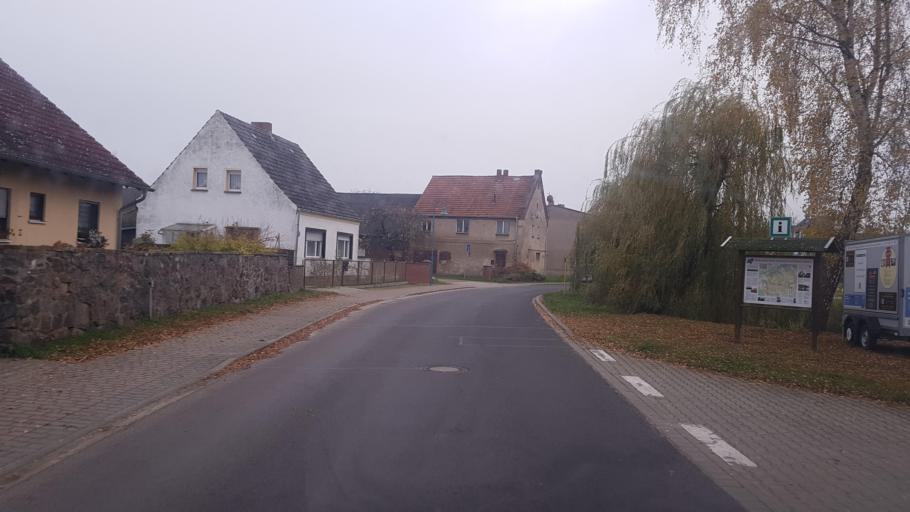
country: DE
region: Brandenburg
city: Gross Kreutz
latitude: 52.3824
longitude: 12.7927
